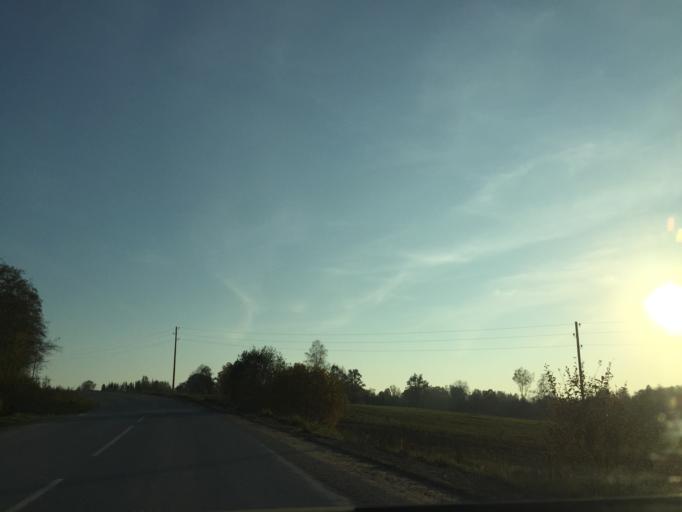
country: LV
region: Vainode
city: Vainode
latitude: 56.5564
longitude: 21.8404
